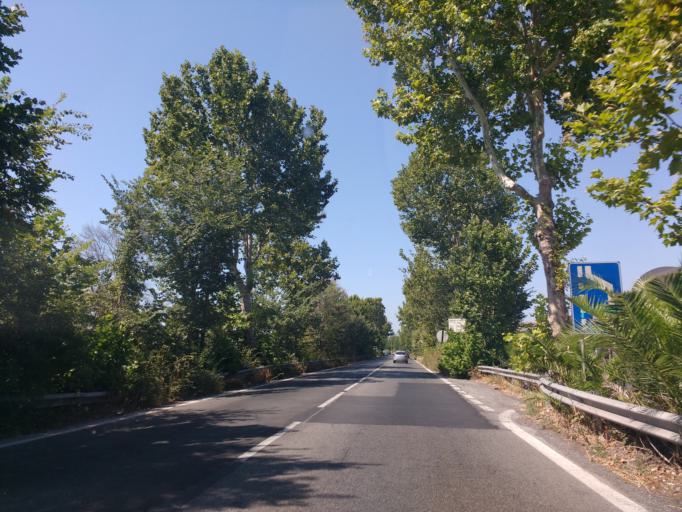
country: IT
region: Latium
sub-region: Citta metropolitana di Roma Capitale
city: Acilia-Castel Fusano-Ostia Antica
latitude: 41.7636
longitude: 12.3097
